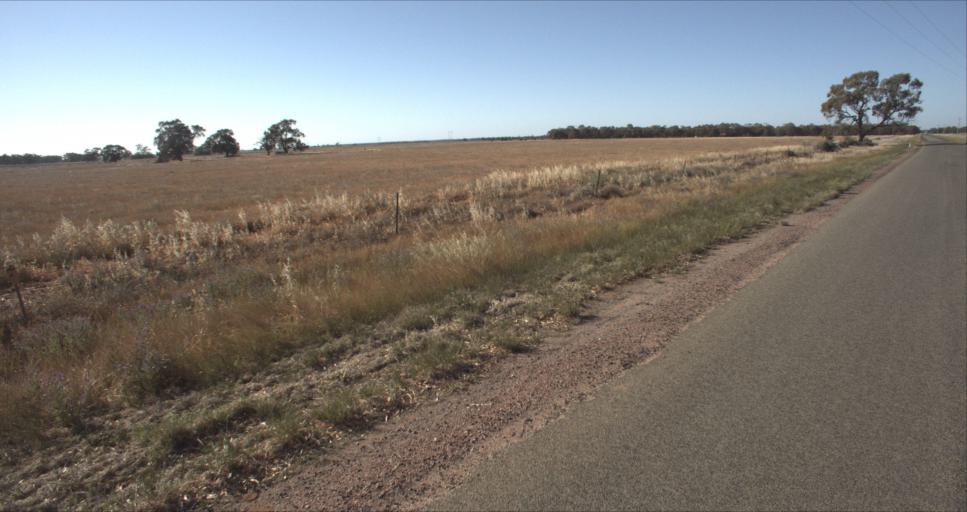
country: AU
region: New South Wales
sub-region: Leeton
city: Leeton
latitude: -34.5554
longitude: 146.2665
